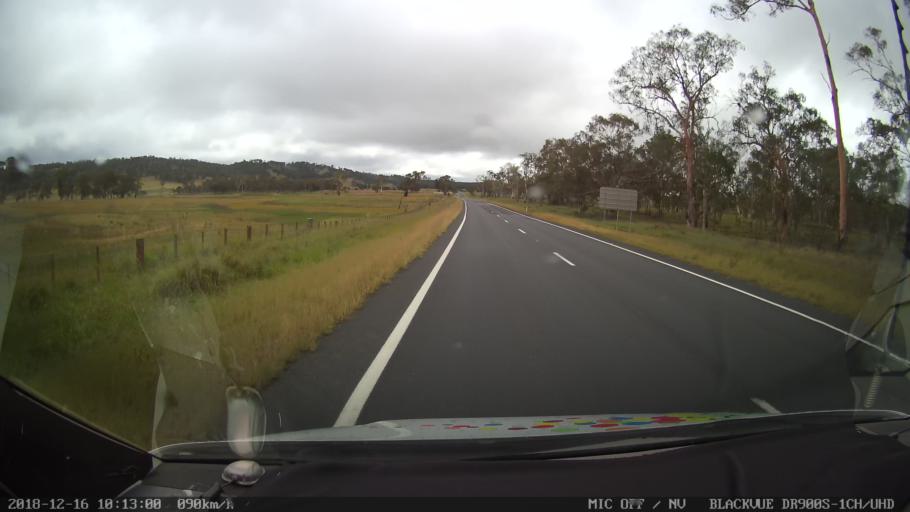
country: AU
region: New South Wales
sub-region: Glen Innes Severn
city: Glen Innes
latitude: -29.3011
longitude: 151.9477
